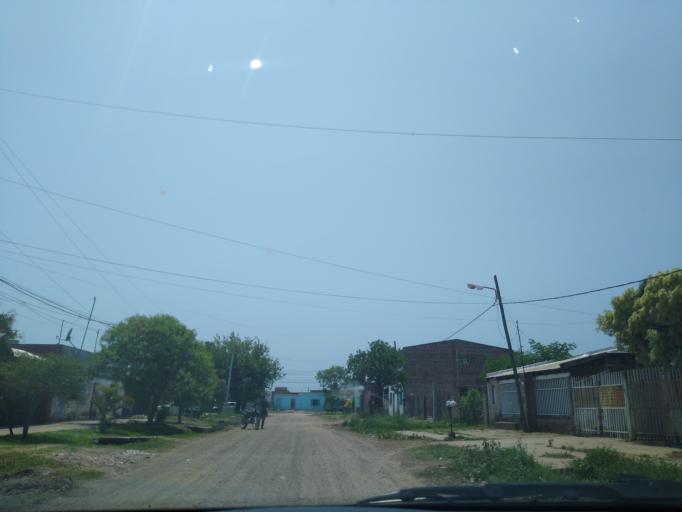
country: AR
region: Chaco
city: Barranqueras
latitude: -27.4748
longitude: -58.9307
